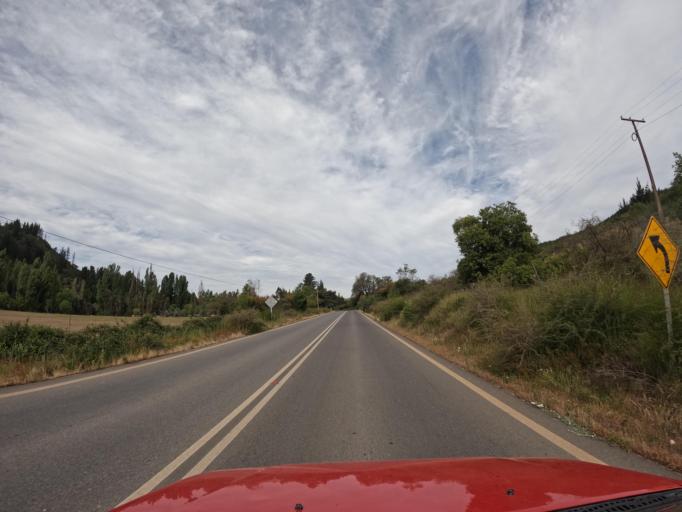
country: CL
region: Maule
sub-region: Provincia de Talca
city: Talca
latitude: -35.3229
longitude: -71.9413
